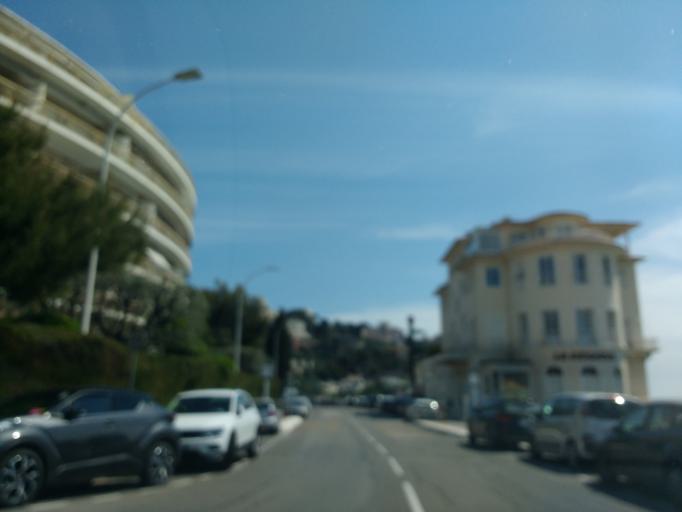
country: FR
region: Provence-Alpes-Cote d'Azur
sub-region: Departement des Alpes-Maritimes
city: Villefranche-sur-Mer
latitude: 43.6922
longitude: 7.2909
